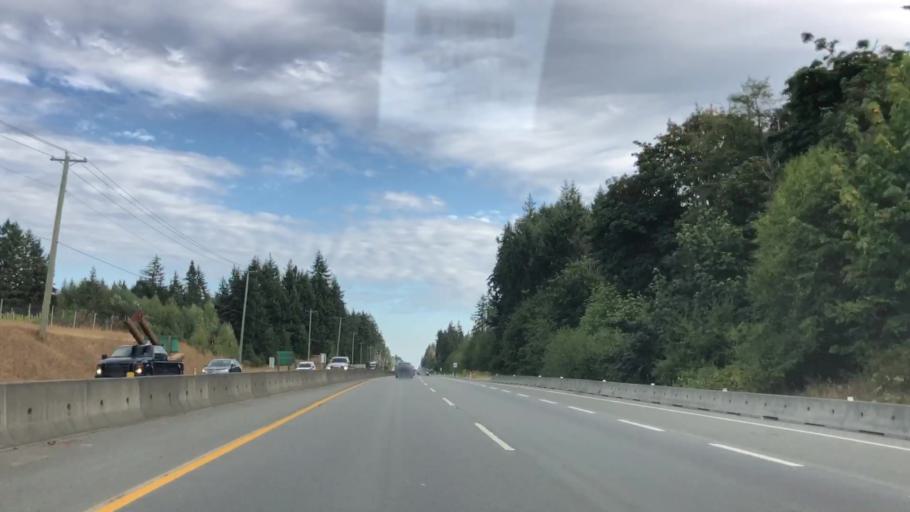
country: CA
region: British Columbia
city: Duncan
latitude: 48.7061
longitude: -123.6057
